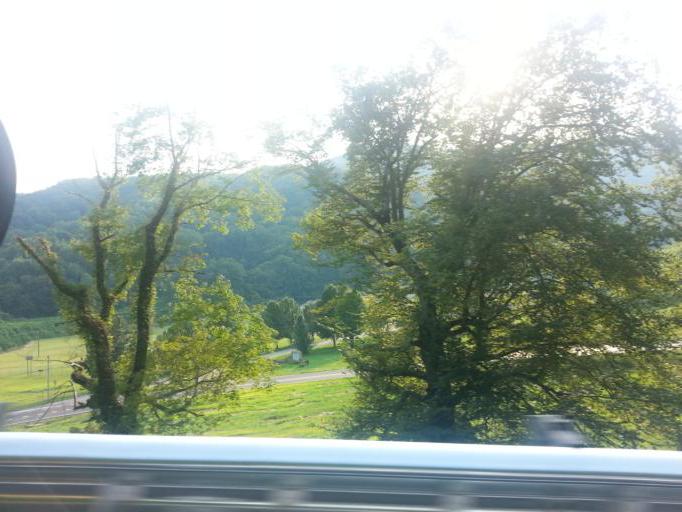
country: US
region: Tennessee
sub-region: Morgan County
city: Coalfield
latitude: 36.1051
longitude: -84.4476
